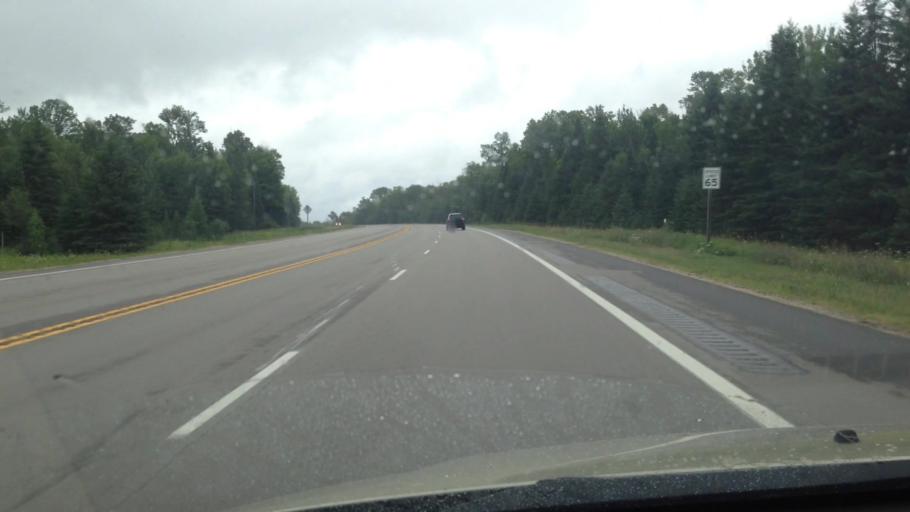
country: US
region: Michigan
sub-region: Schoolcraft County
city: Manistique
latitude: 45.8963
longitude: -86.5016
